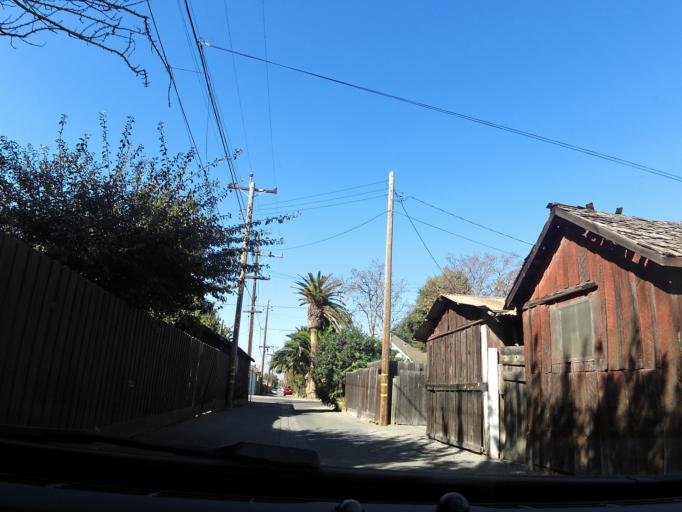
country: US
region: California
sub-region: San Benito County
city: Hollister
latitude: 36.8521
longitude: -121.4071
